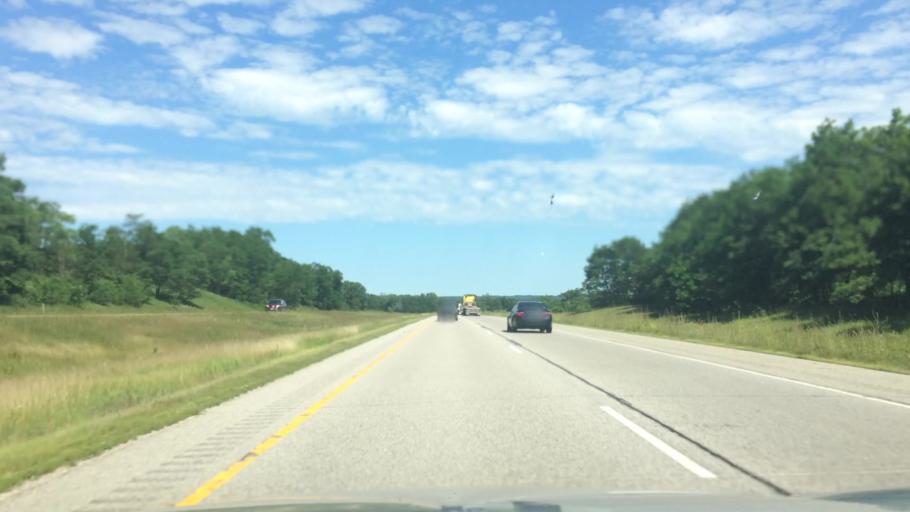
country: US
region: Wisconsin
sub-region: Marquette County
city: Westfield
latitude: 43.7268
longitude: -89.4821
